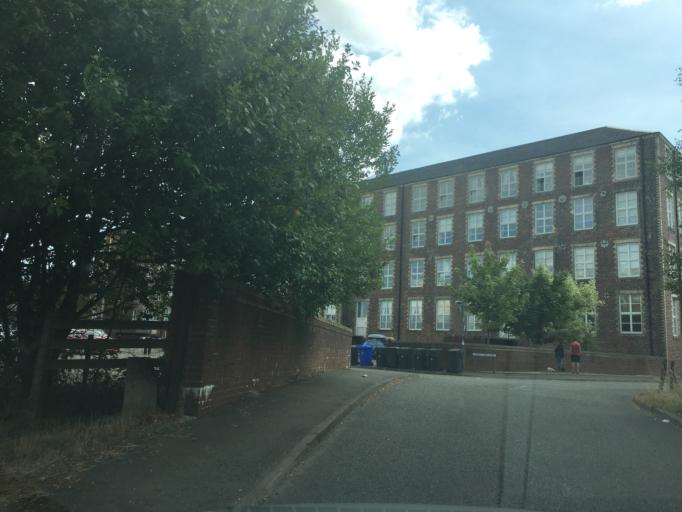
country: GB
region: Scotland
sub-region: Stirling
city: Stirling
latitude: 56.1126
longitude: -3.9727
